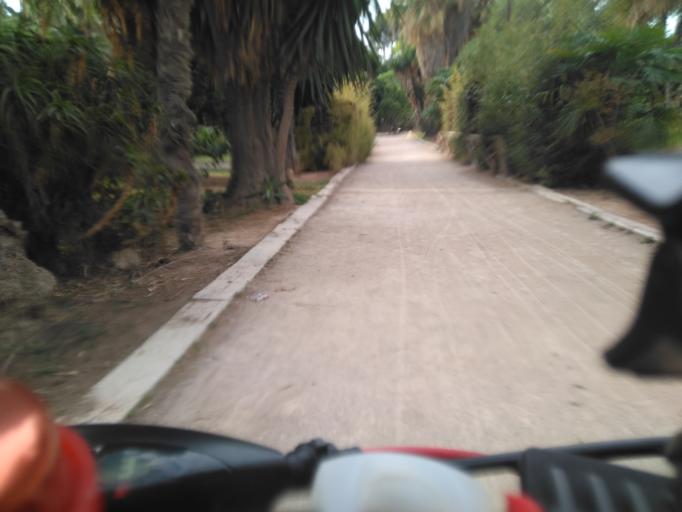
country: ES
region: Valencia
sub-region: Provincia de Valencia
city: Valencia
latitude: 39.4822
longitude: -0.3682
